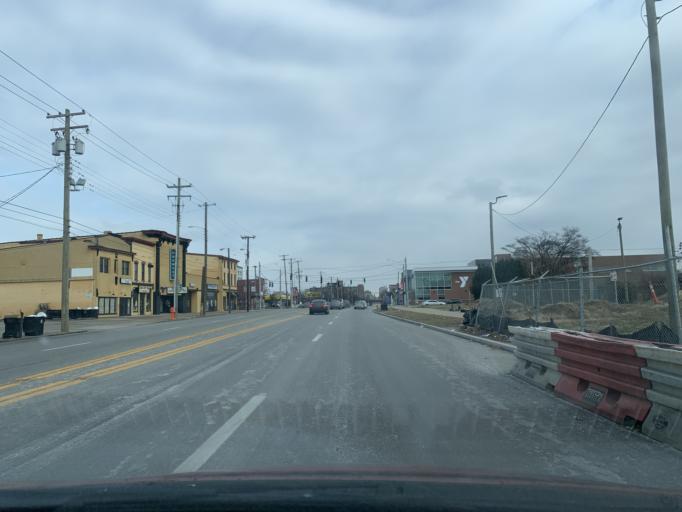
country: US
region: Kentucky
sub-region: Jefferson County
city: Louisville
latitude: 38.2490
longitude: -85.7829
